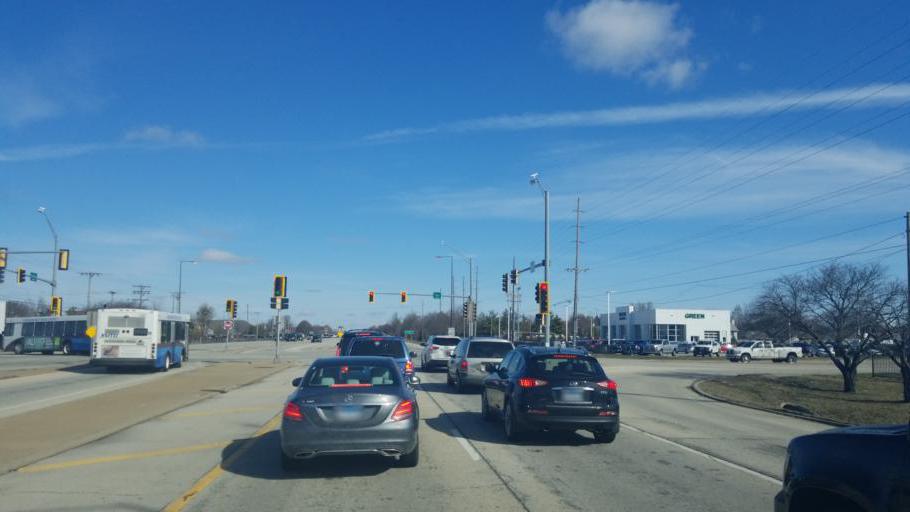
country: US
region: Illinois
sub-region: Sangamon County
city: Jerome
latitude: 39.7695
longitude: -89.7063
